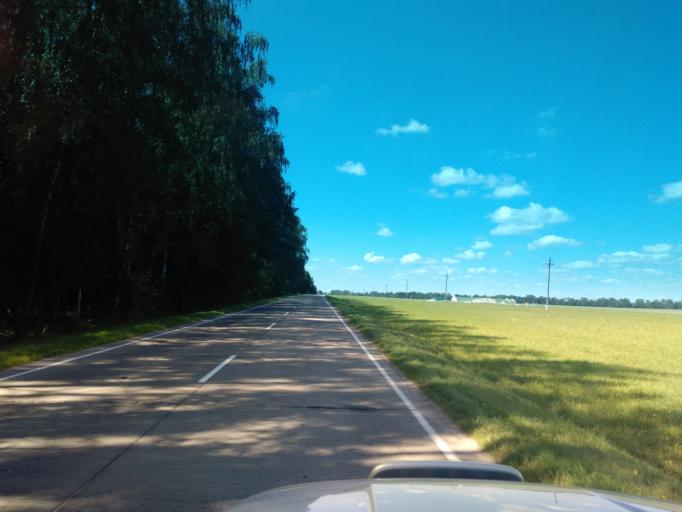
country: BY
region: Minsk
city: Stan'kava
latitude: 53.6235
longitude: 27.2889
